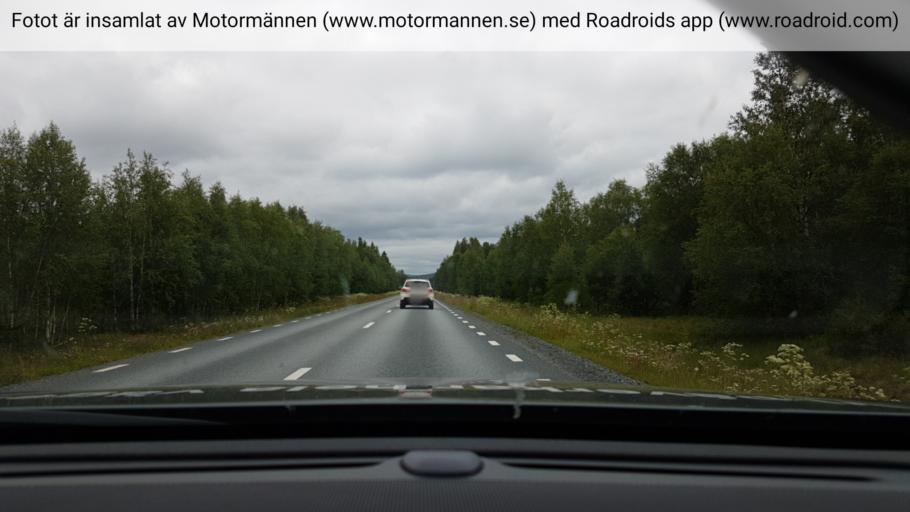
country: SE
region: Vaesterbotten
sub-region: Sorsele Kommun
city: Sorsele
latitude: 65.5166
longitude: 17.5398
